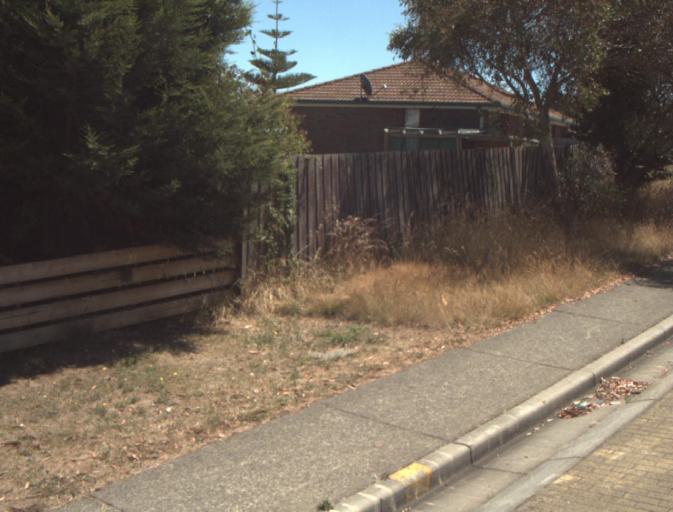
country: AU
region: Tasmania
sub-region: Launceston
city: Mayfield
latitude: -41.3783
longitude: 147.1355
